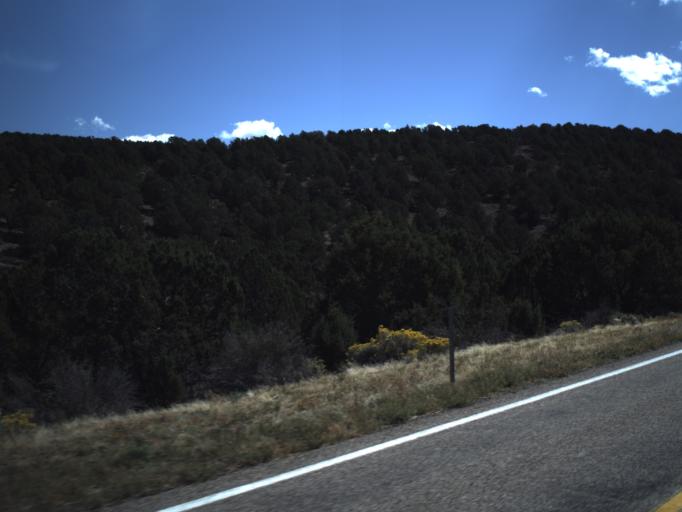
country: US
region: Utah
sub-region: Washington County
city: Enterprise
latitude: 37.5569
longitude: -113.6902
